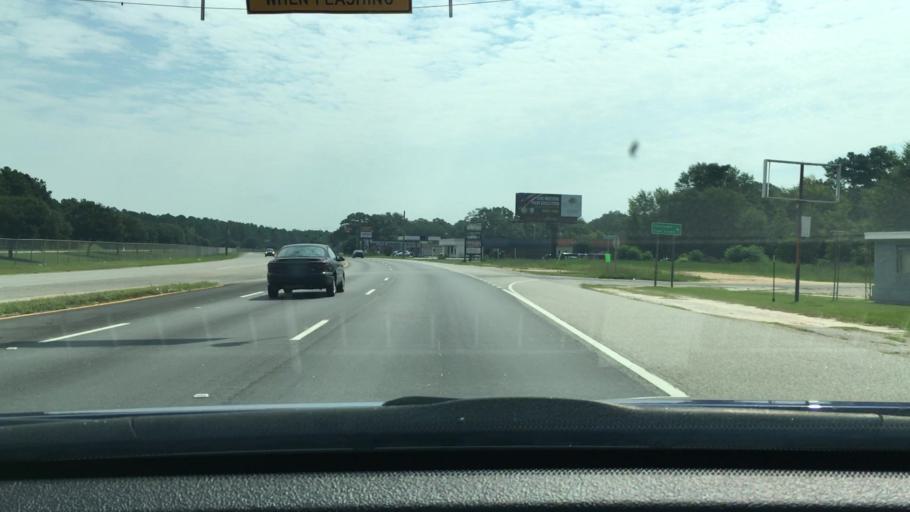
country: US
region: South Carolina
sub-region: Sumter County
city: Cherryvale
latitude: 33.9614
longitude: -80.4681
